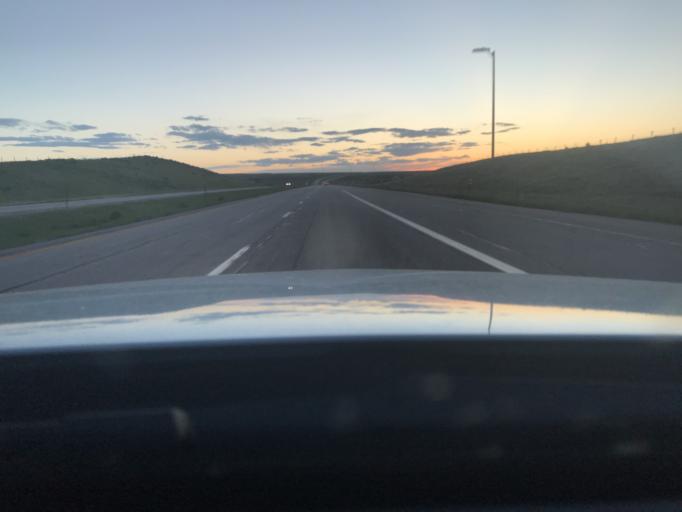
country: US
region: Wyoming
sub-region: Converse County
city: Glenrock
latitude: 42.8248
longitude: -105.8026
